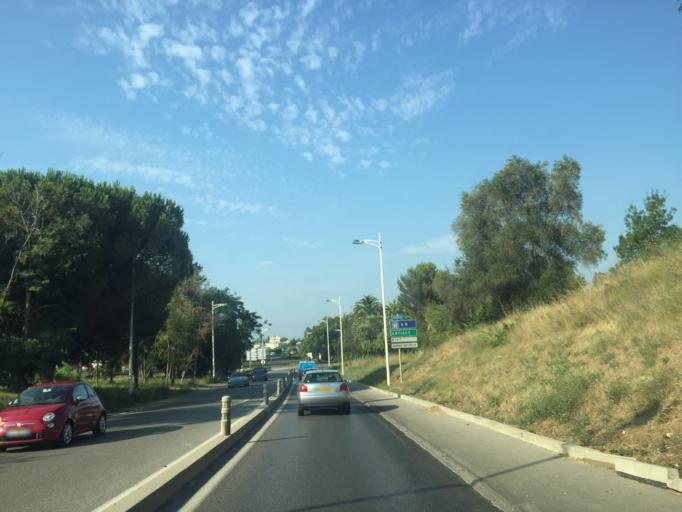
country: FR
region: Provence-Alpes-Cote d'Azur
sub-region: Departement des Alpes-Maritimes
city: Cagnes-sur-Mer
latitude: 43.6507
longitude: 7.1413
